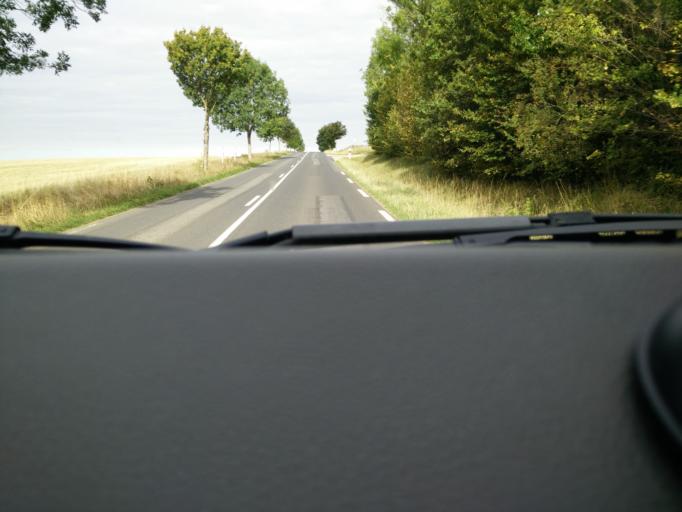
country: FR
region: Lorraine
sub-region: Departement de Meurthe-et-Moselle
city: Montauville
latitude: 48.8961
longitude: 5.9731
